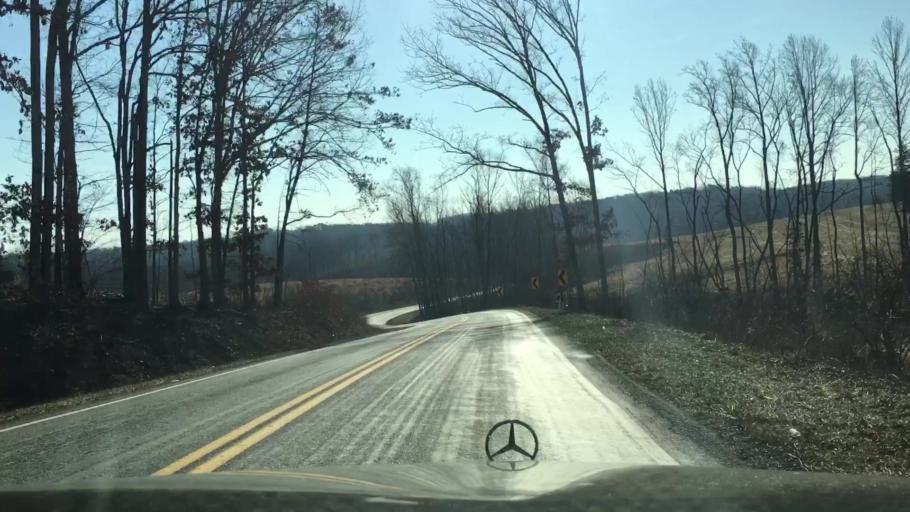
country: US
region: Virginia
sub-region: Campbell County
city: Altavista
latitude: 37.1520
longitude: -79.3397
